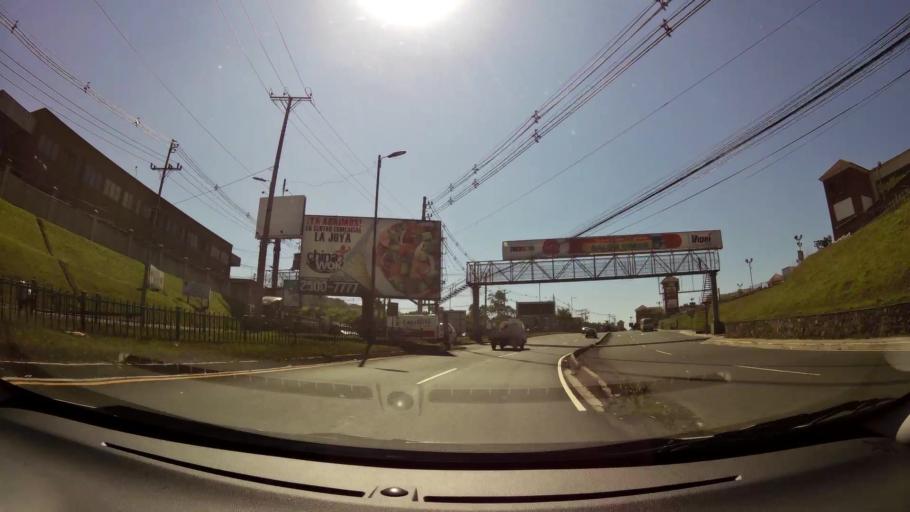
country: SV
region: La Libertad
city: Nuevo Cuscatlan
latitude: 13.6583
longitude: -89.2786
